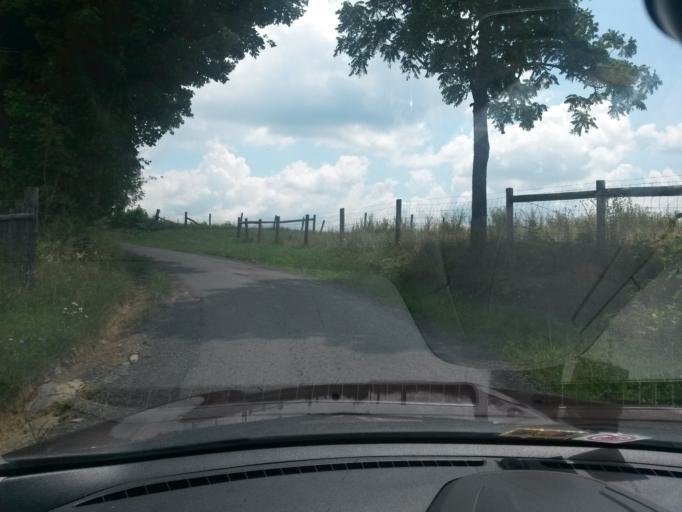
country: US
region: West Virginia
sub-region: Monroe County
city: Union
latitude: 37.5594
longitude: -80.5122
